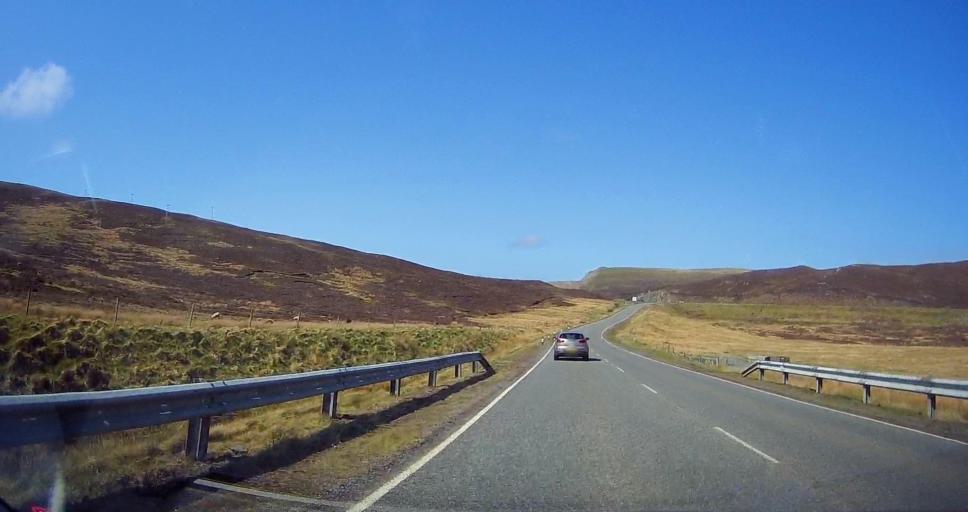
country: GB
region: Scotland
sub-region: Shetland Islands
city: Lerwick
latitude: 60.1409
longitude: -1.2380
